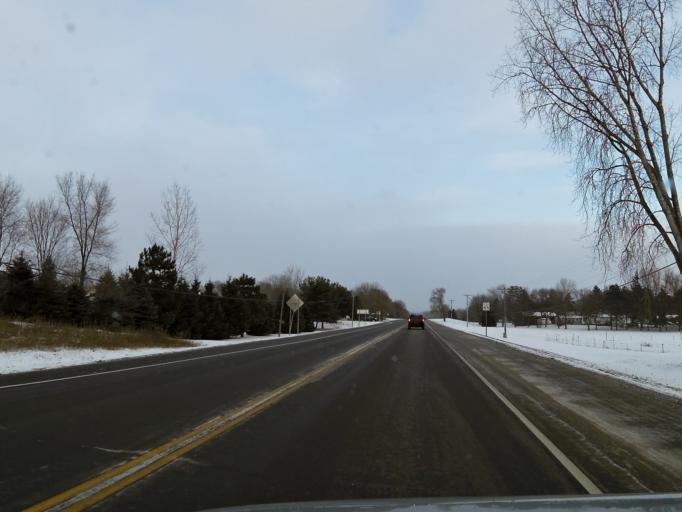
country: US
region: Minnesota
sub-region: Washington County
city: Lake Elmo
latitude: 44.9635
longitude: -92.8817
